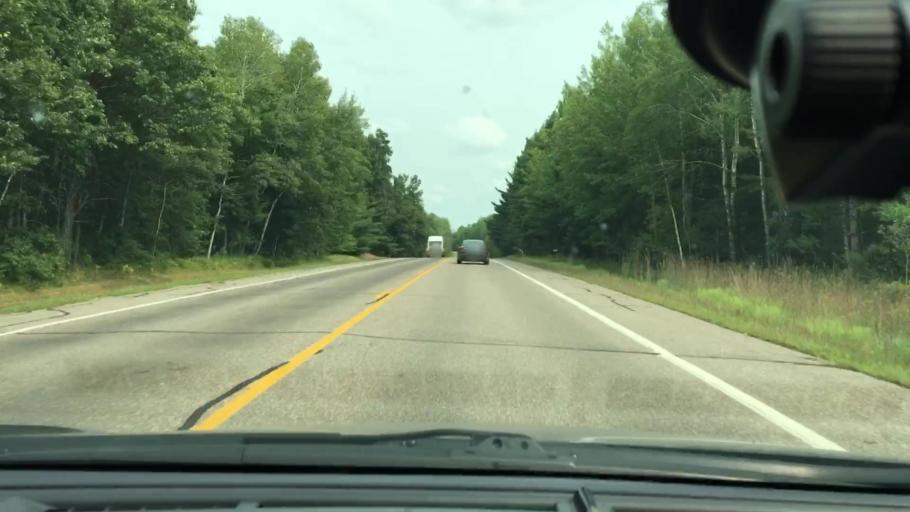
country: US
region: Minnesota
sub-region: Crow Wing County
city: Cross Lake
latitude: 46.7310
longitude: -94.0120
